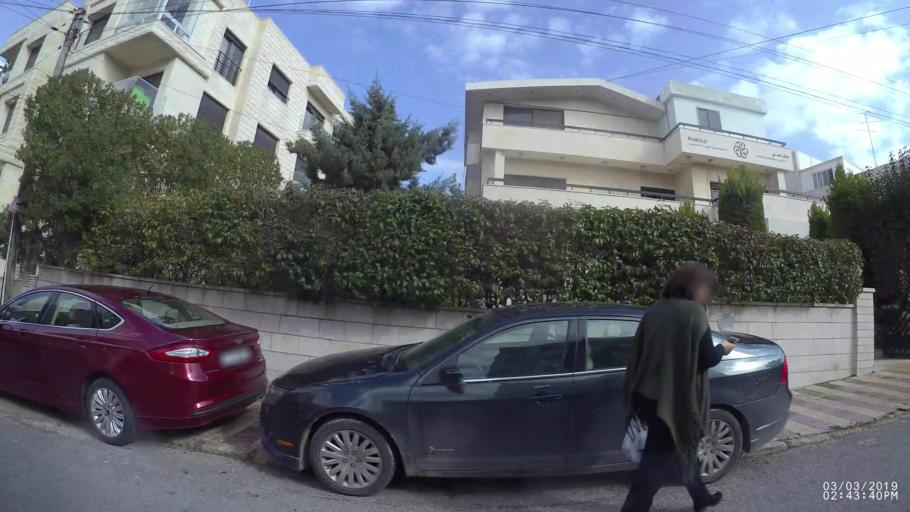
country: JO
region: Amman
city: Amman
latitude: 31.9653
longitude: 35.8898
